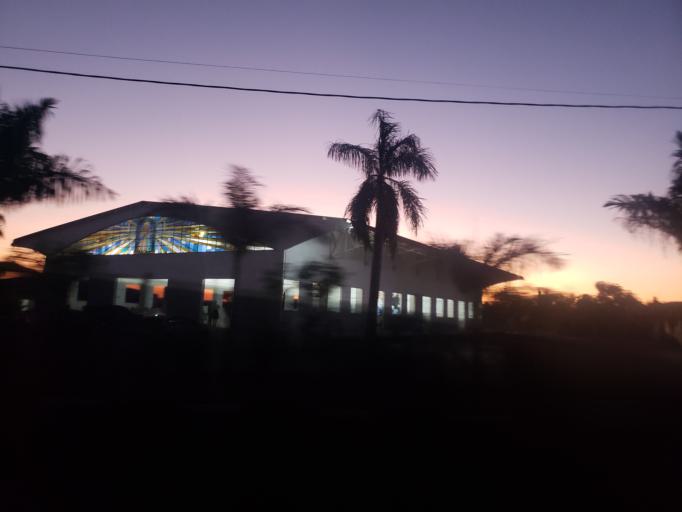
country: BR
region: Sao Paulo
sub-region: Conchal
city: Conchal
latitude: -22.2909
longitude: -47.1346
